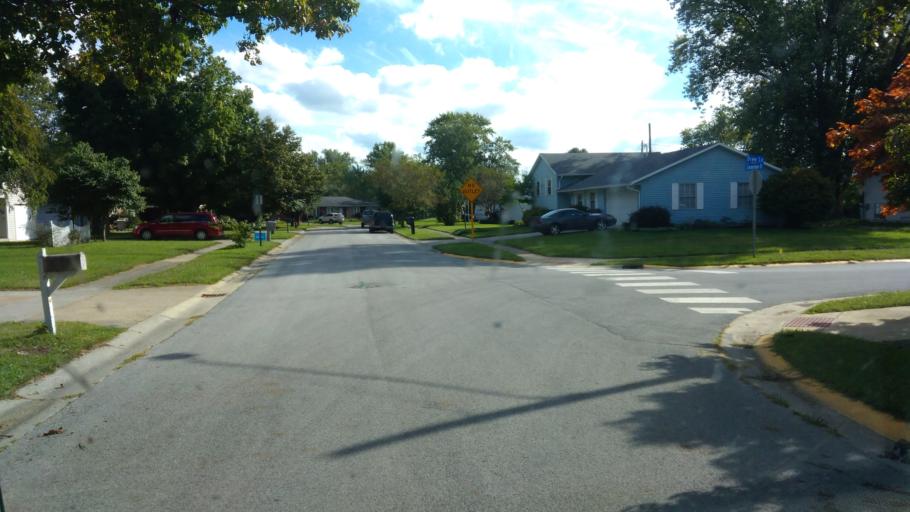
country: US
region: Ohio
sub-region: Sandusky County
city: Clyde
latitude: 41.2930
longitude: -82.9828
